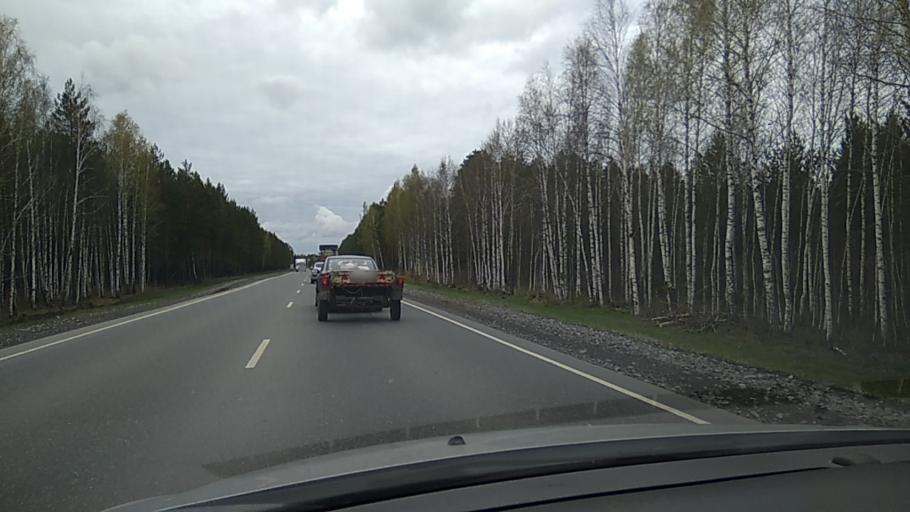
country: RU
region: Tjumen
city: Chervishevo
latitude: 57.0030
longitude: 65.4866
